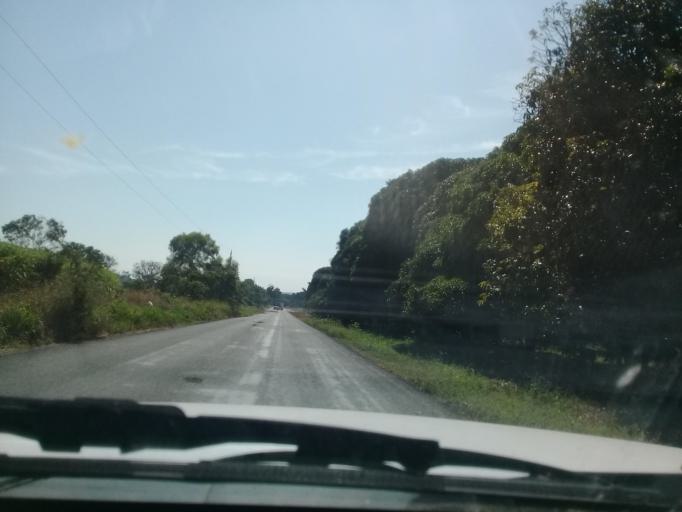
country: MX
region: Veracruz
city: Actopan
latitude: 19.4648
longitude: -96.5750
